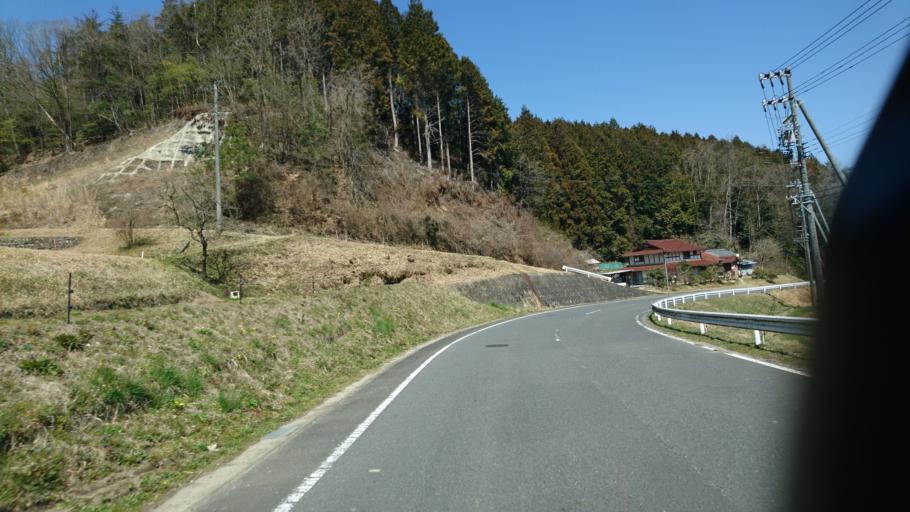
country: JP
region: Gifu
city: Nakatsugawa
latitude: 35.4609
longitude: 137.3751
